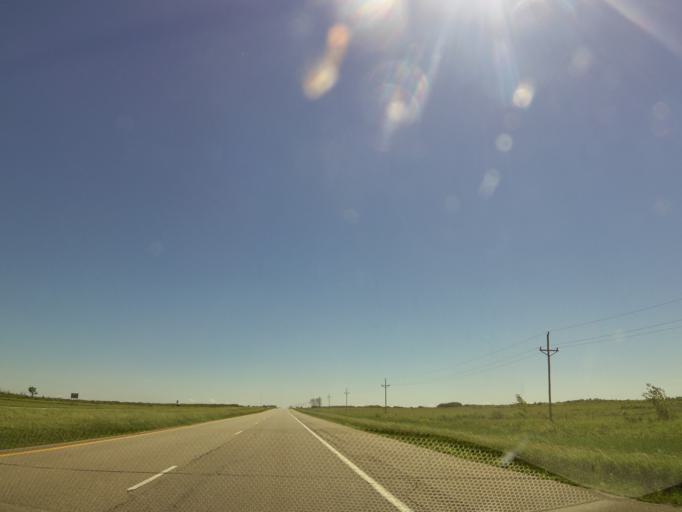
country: US
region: Minnesota
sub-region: Red Lake County
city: Red Lake Falls
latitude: 47.7603
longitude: -96.3927
